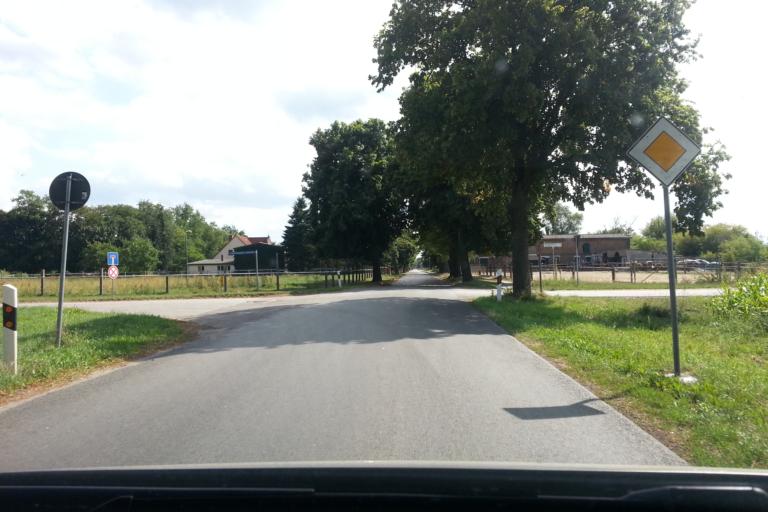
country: DE
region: Mecklenburg-Vorpommern
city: Ferdinandshof
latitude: 53.6450
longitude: 13.8748
